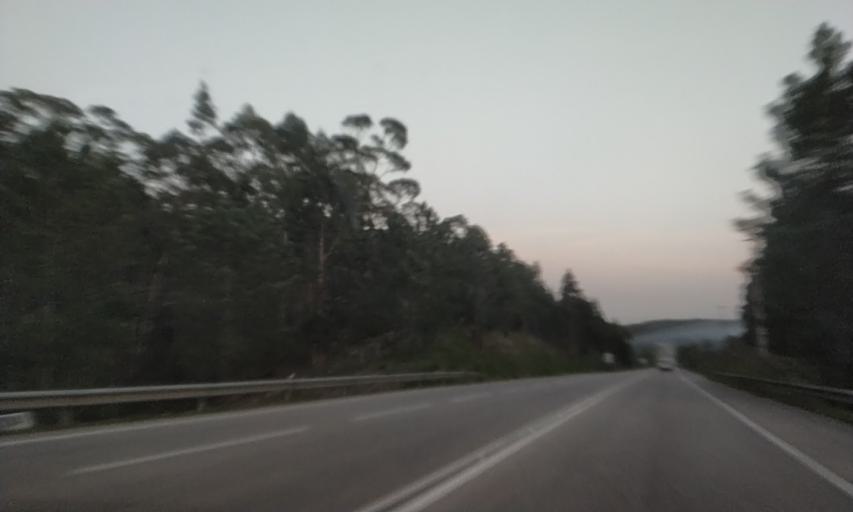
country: PT
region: Leiria
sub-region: Leiria
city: Leiria
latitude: 39.7469
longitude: -8.8547
